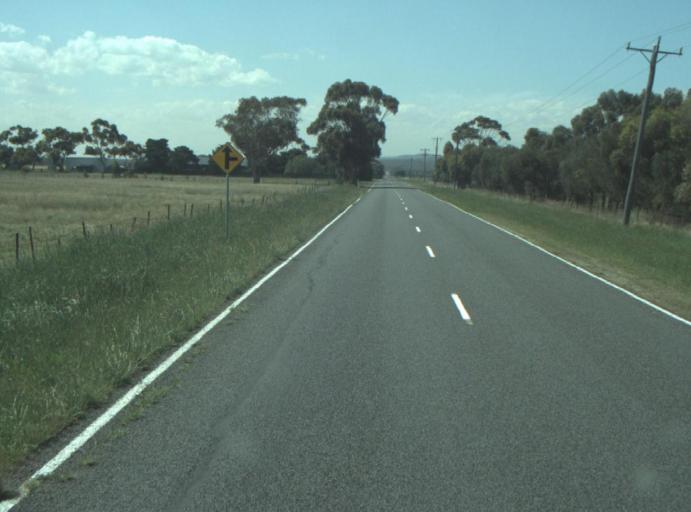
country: AU
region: Victoria
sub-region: Greater Geelong
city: Lara
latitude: -37.9959
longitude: 144.4012
